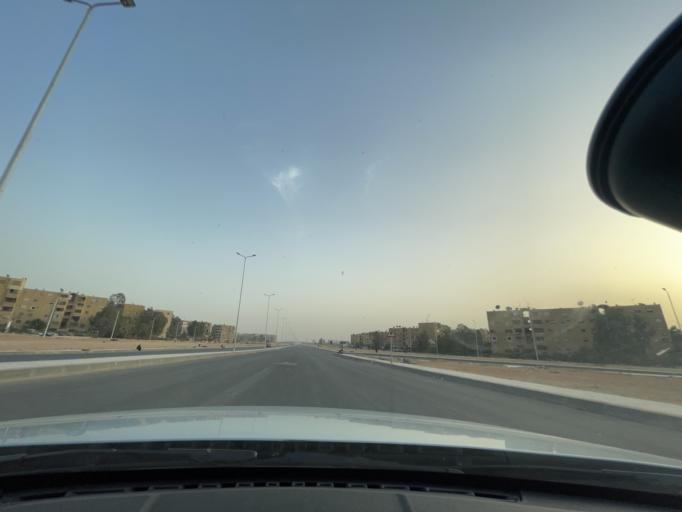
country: EG
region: Muhafazat al Qahirah
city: Cairo
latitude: 30.0462
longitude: 31.3644
